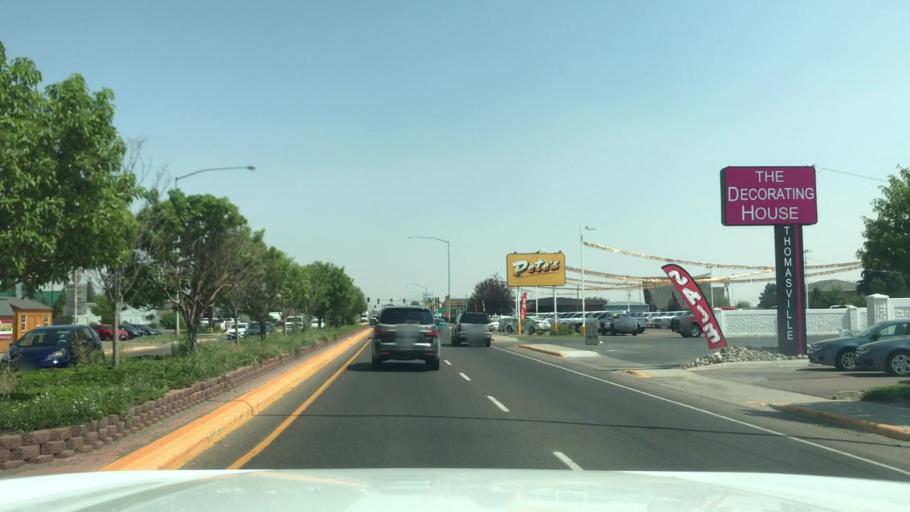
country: US
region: Montana
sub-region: Cascade County
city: Great Falls
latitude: 47.4940
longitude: -111.2448
